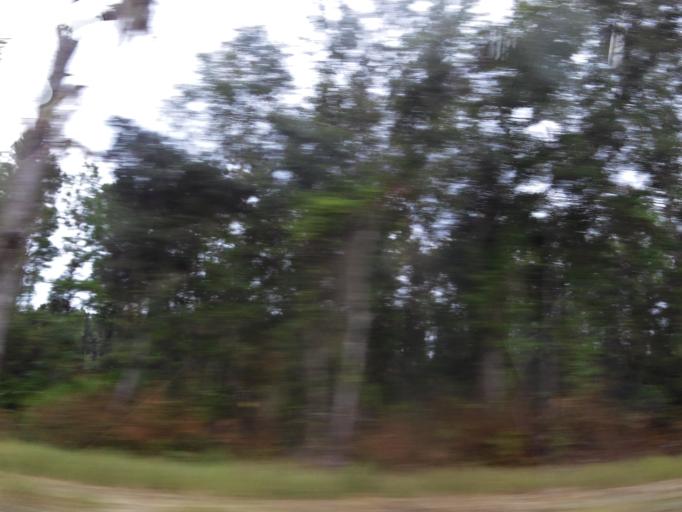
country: US
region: Georgia
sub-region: McIntosh County
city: Darien
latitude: 31.4307
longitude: -81.6750
